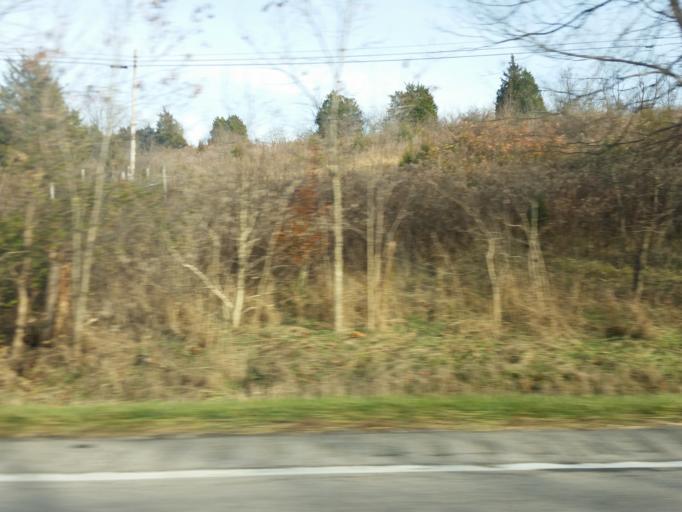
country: US
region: Kentucky
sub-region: Harrison County
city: Cynthiana
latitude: 38.4586
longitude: -84.2856
